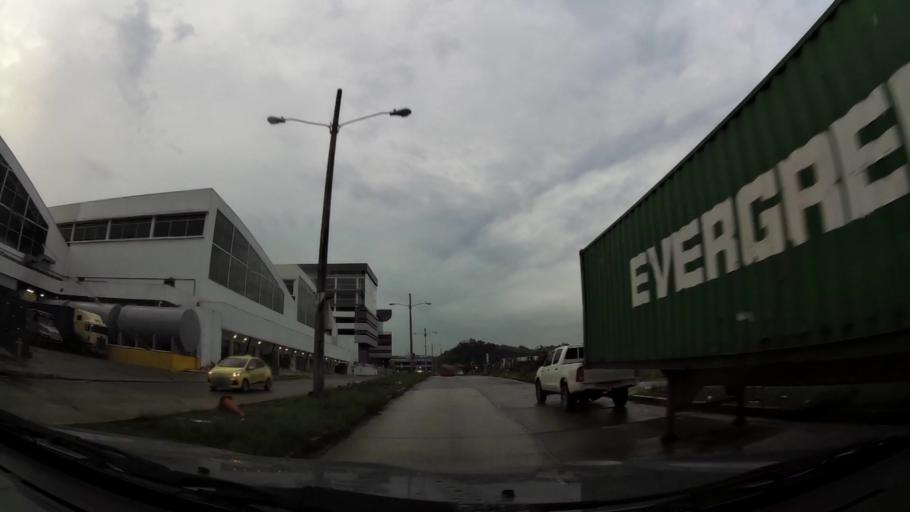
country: PA
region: Panama
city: Panama
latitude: 9.0314
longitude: -79.5314
